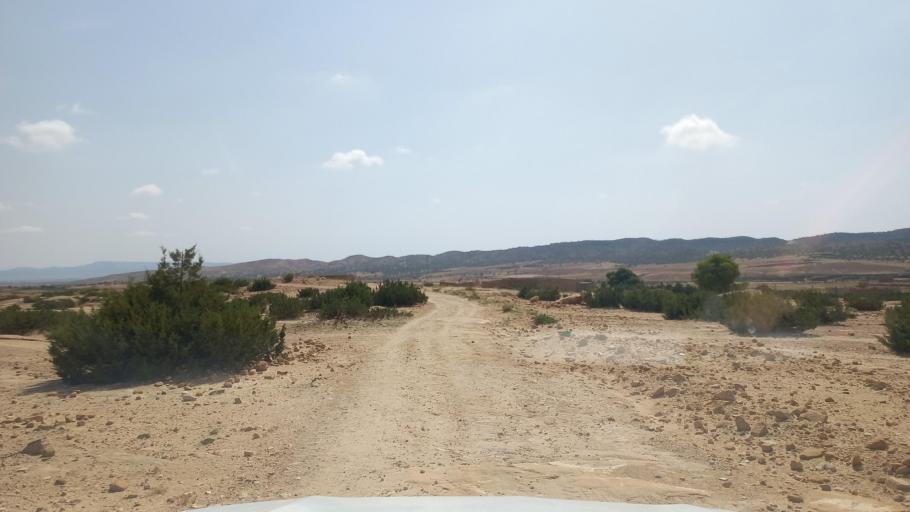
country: TN
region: Al Qasrayn
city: Sbiba
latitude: 35.3983
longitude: 8.9598
